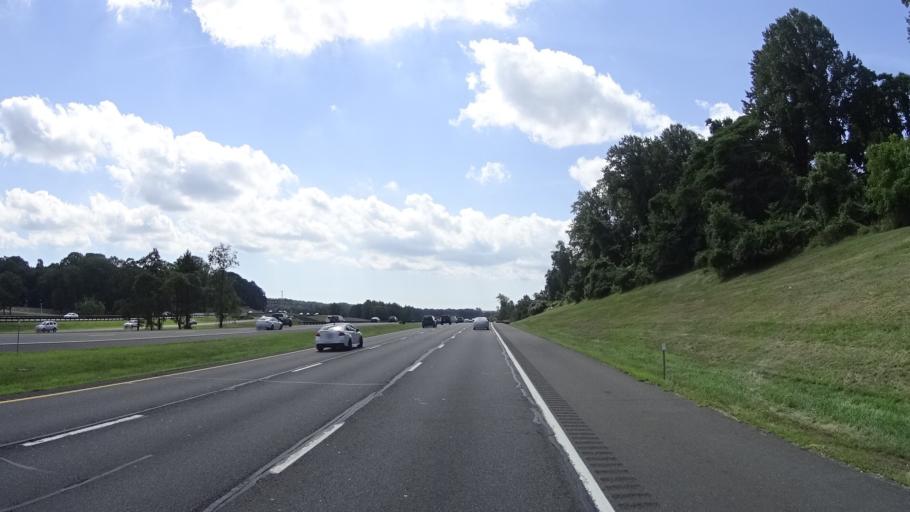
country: US
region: New Jersey
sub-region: Monmouth County
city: Strathmore
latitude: 40.3908
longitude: -74.1811
